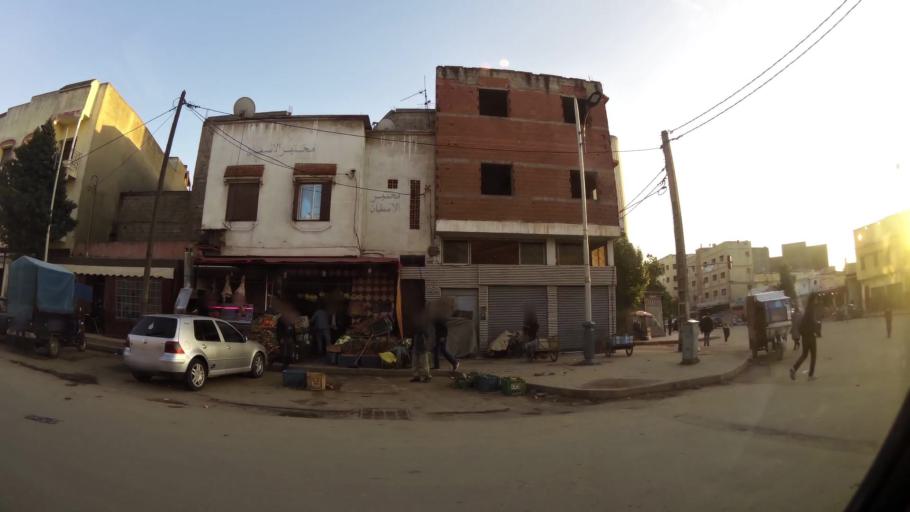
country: MA
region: Chaouia-Ouardigha
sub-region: Settat Province
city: Settat
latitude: 33.0000
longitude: -7.6167
